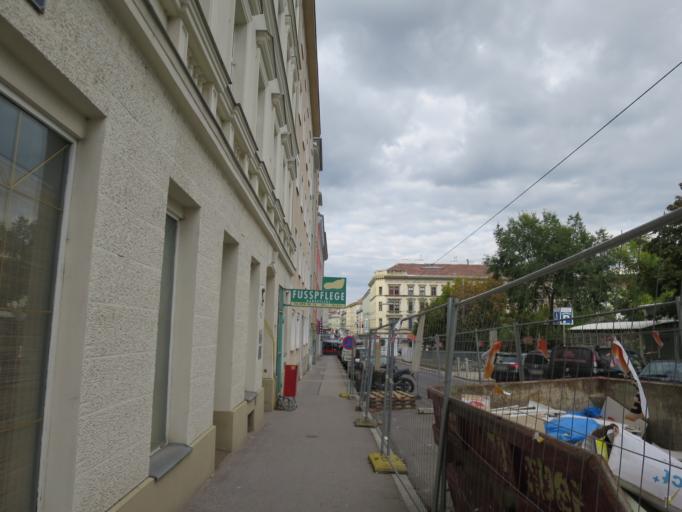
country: AT
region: Vienna
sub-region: Wien Stadt
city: Vienna
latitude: 48.2085
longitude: 16.3326
